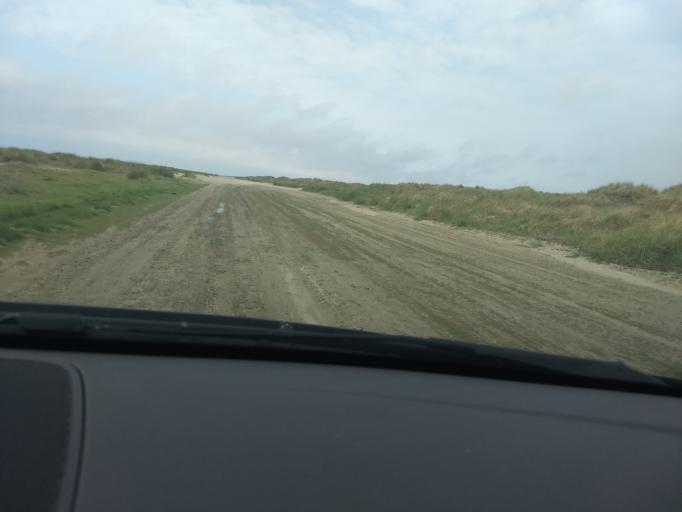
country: DK
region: South Denmark
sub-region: Fano Kommune
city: Nordby
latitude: 55.4097
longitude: 8.3852
